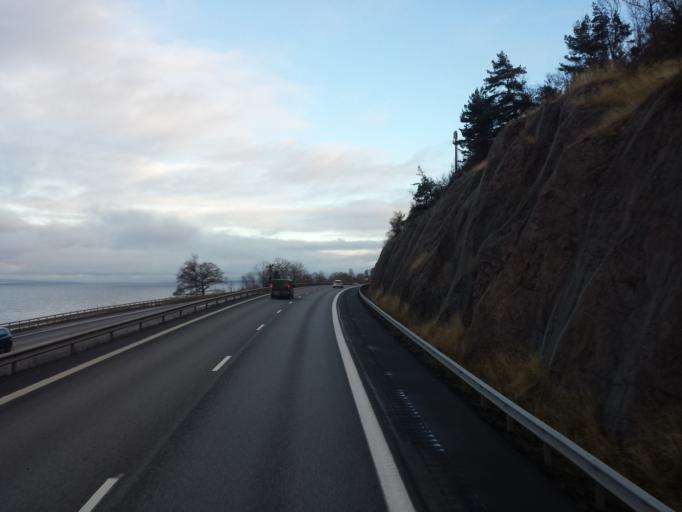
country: SE
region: Joenkoeping
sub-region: Jonkopings Kommun
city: Kaxholmen
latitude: 57.8689
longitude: 14.2715
